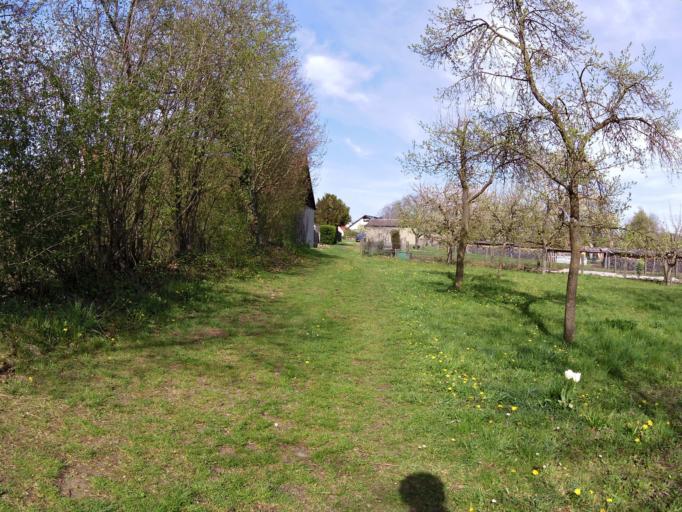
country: DE
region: Bavaria
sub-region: Regierungsbezirk Unterfranken
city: Unterpleichfeld
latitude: 49.8706
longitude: 10.0314
